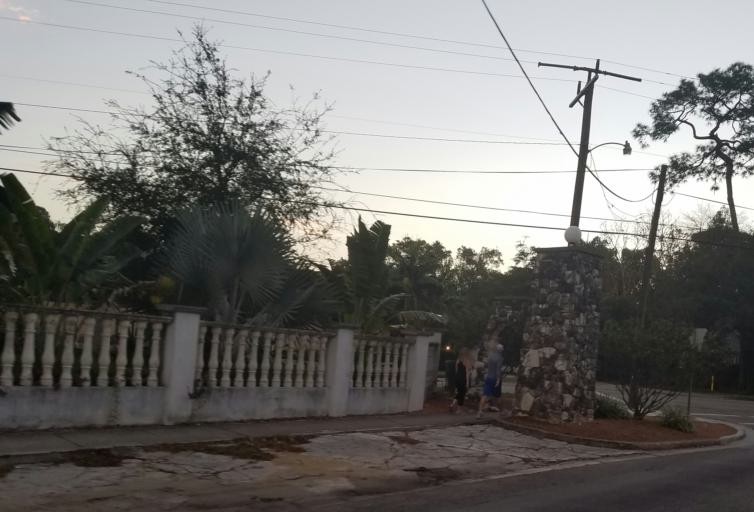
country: US
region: Florida
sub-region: Sarasota County
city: Siesta Key
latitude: 27.3121
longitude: -82.5349
